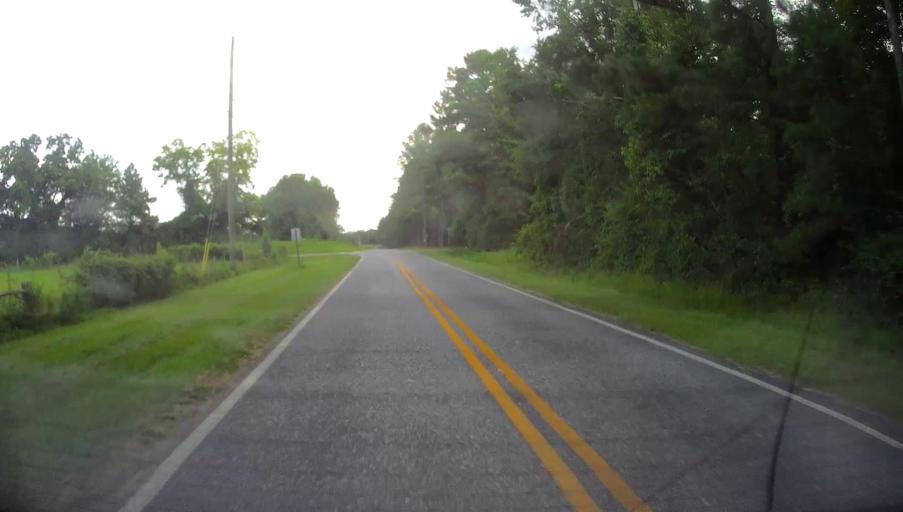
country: US
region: Georgia
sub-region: Crawford County
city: Roberta
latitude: 32.7029
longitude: -84.0164
